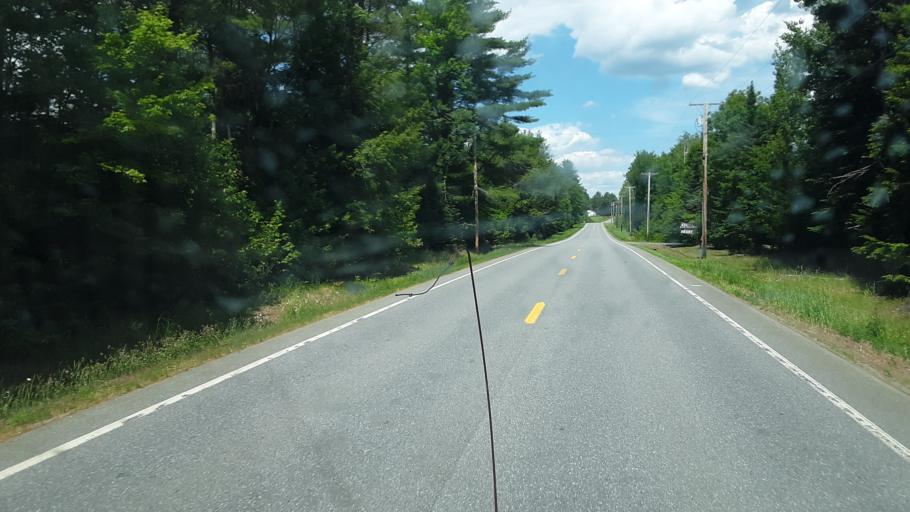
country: US
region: Maine
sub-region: Franklin County
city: Chesterville
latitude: 44.6061
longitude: -70.1024
